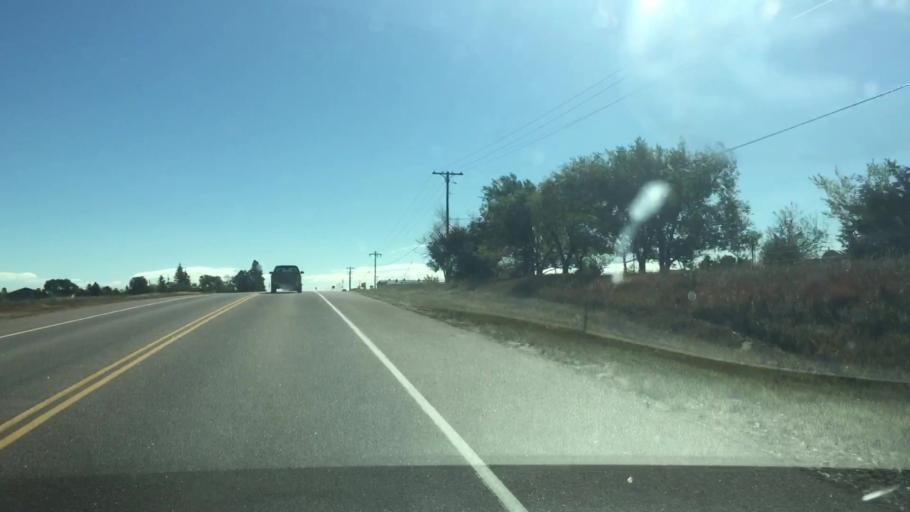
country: US
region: Colorado
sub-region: Elbert County
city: Kiowa
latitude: 39.3566
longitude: -104.5244
